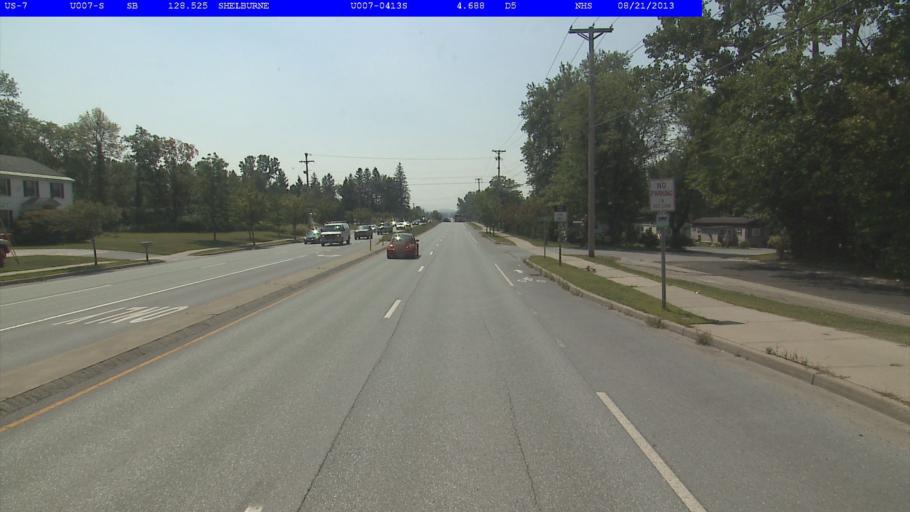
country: US
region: Vermont
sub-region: Chittenden County
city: Burlington
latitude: 44.4168
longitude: -73.2133
